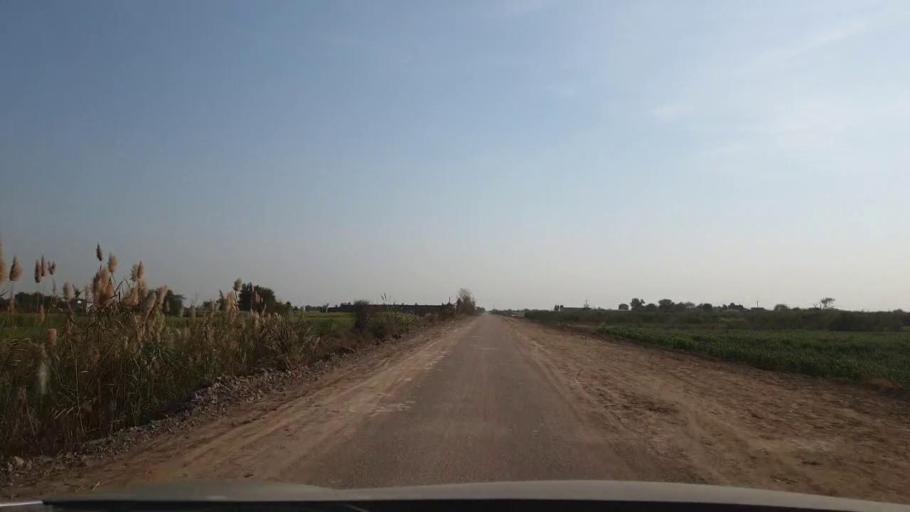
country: PK
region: Sindh
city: Berani
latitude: 25.7312
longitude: 68.8066
